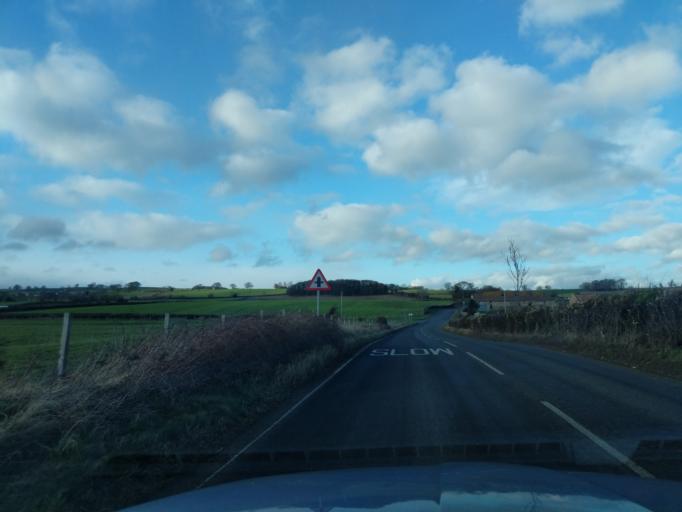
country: GB
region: England
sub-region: North Yorkshire
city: Catterick Garrison
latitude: 54.3336
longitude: -1.6857
